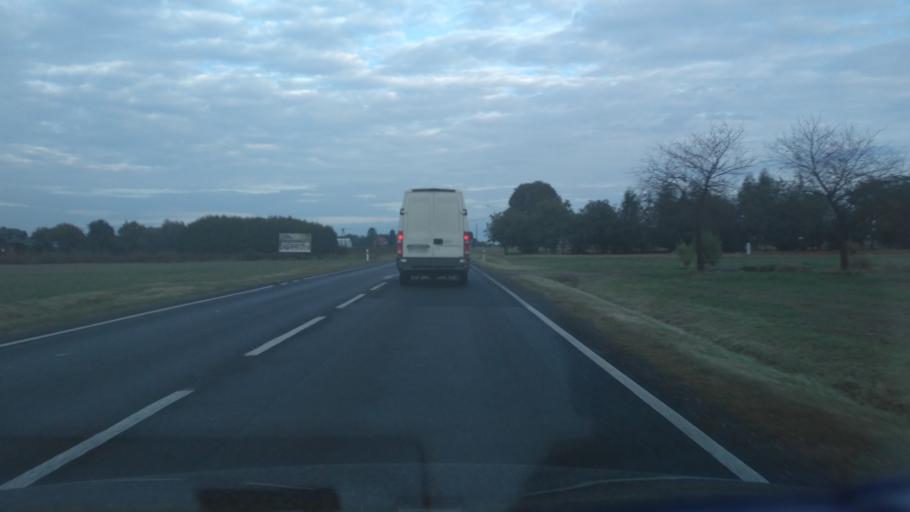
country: PL
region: Lublin Voivodeship
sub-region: Powiat leczynski
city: Spiczyn
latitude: 51.2985
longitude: 22.7680
